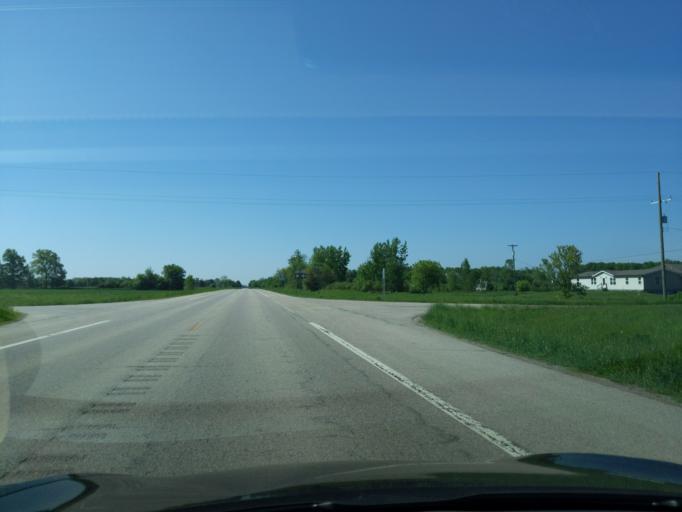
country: US
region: Michigan
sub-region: Ingham County
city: Stockbridge
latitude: 42.5409
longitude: -84.1913
